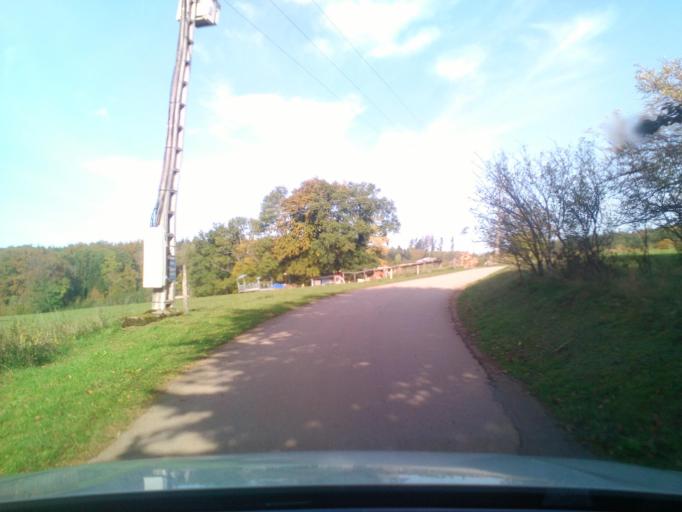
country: FR
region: Lorraine
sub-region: Departement des Vosges
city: Senones
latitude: 48.3879
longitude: 7.0576
